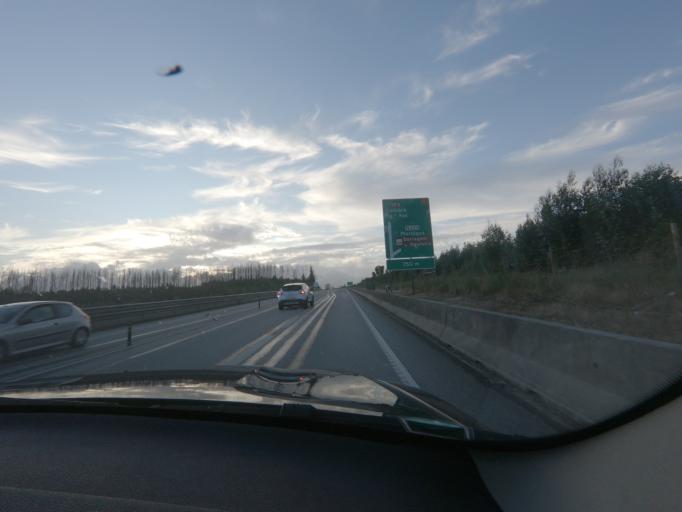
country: PT
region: Viseu
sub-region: Mortagua
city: Mortagua
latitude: 40.3504
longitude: -8.1883
